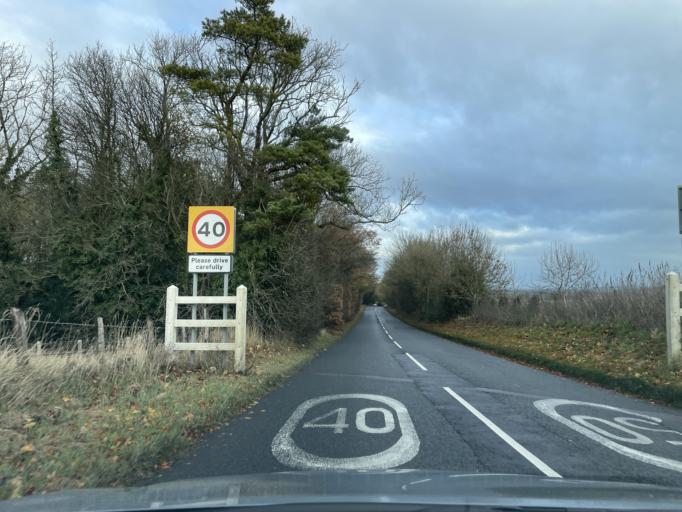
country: GB
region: England
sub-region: Borough of Swindon
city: Wroughton
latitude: 51.5168
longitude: -1.8091
